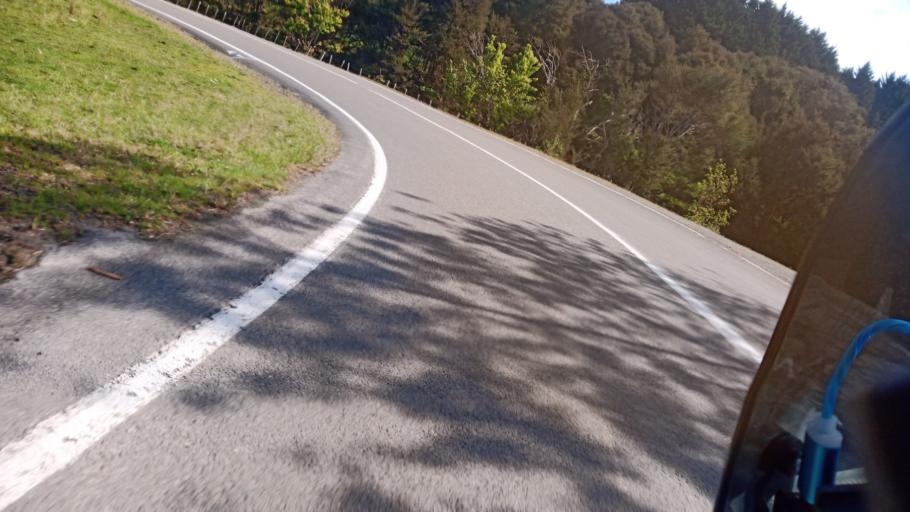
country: NZ
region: Gisborne
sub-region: Gisborne District
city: Gisborne
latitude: -37.8643
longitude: 178.1991
